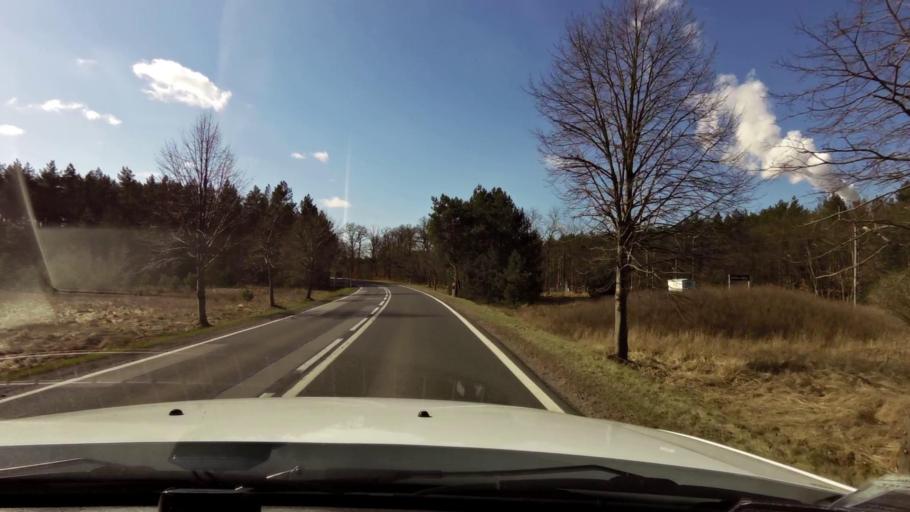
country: PL
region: West Pomeranian Voivodeship
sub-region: Powiat gryfinski
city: Gryfino
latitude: 53.2107
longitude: 14.4813
